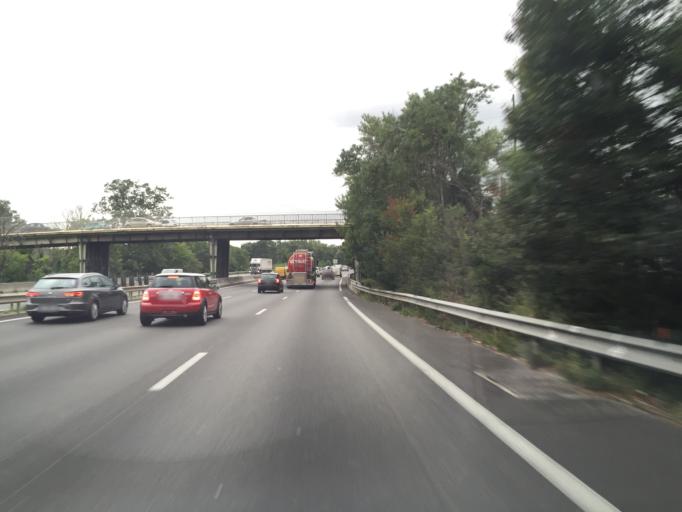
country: FR
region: Provence-Alpes-Cote d'Azur
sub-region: Departement des Alpes-Maritimes
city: Biot
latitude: 43.6175
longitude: 7.1153
